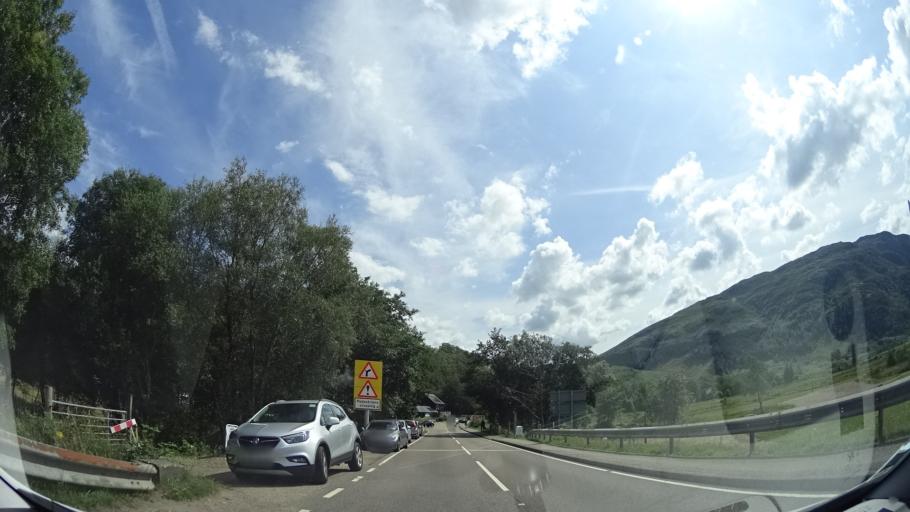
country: GB
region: Scotland
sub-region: Highland
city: Fort William
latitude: 56.8710
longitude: -5.4369
